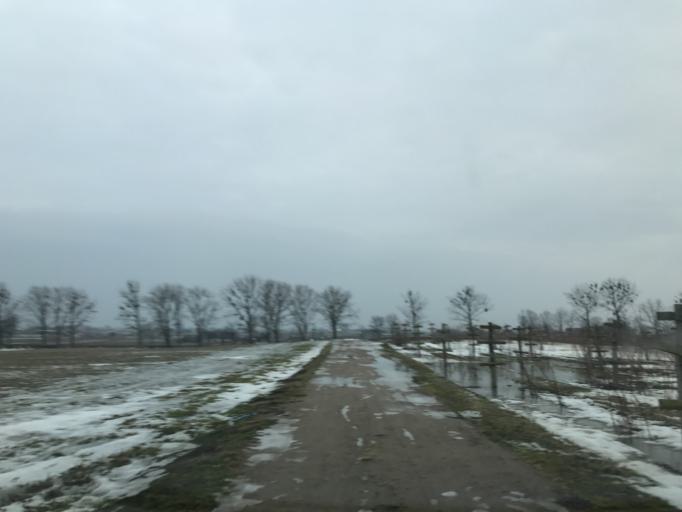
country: PL
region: Kujawsko-Pomorskie
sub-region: Powiat brodnicki
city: Bartniczka
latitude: 53.2256
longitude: 19.6071
